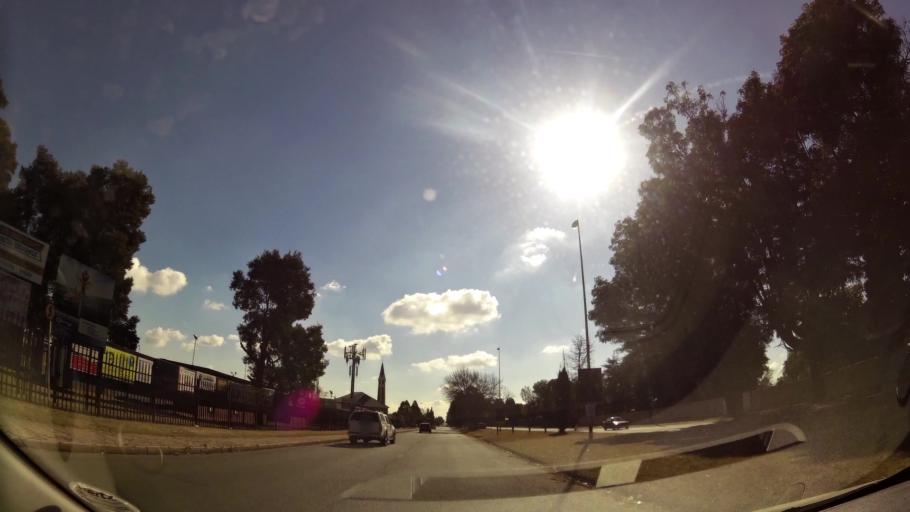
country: ZA
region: Gauteng
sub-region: City of Johannesburg Metropolitan Municipality
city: Roodepoort
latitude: -26.1390
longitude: 27.8363
